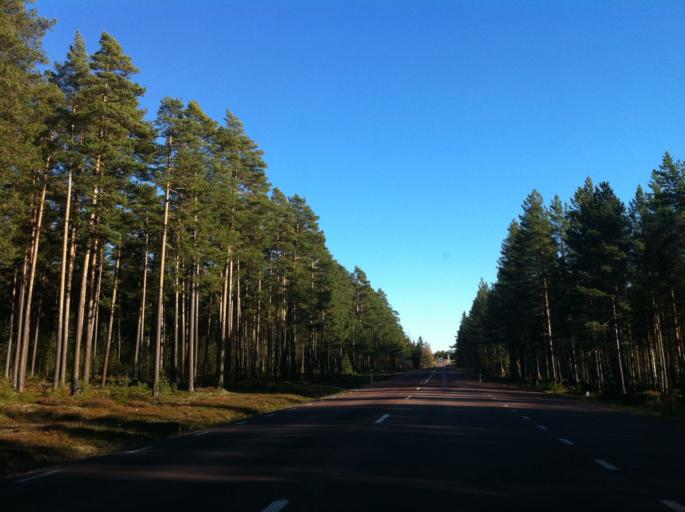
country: SE
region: Dalarna
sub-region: Leksand Municipality
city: Siljansnas
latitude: 60.9277
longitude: 14.8023
